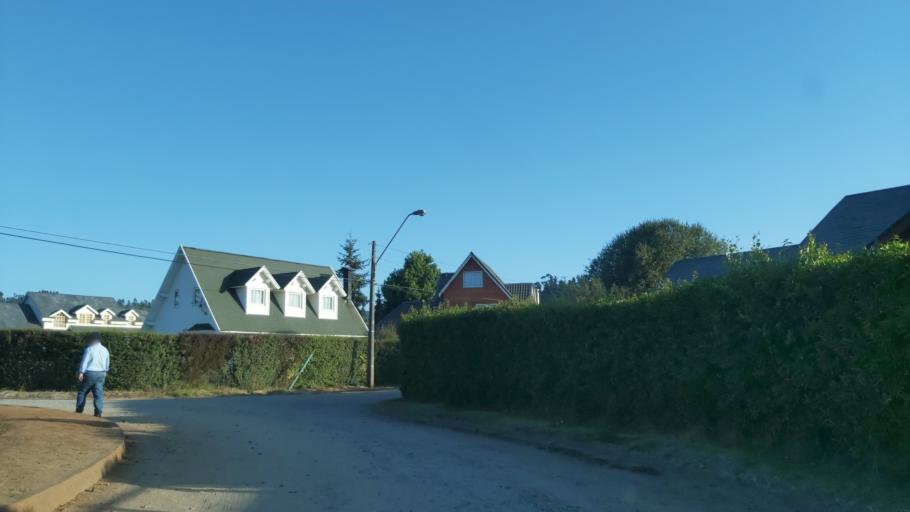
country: CL
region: Biobio
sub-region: Provincia de Concepcion
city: Tome
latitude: -36.5301
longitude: -72.9326
